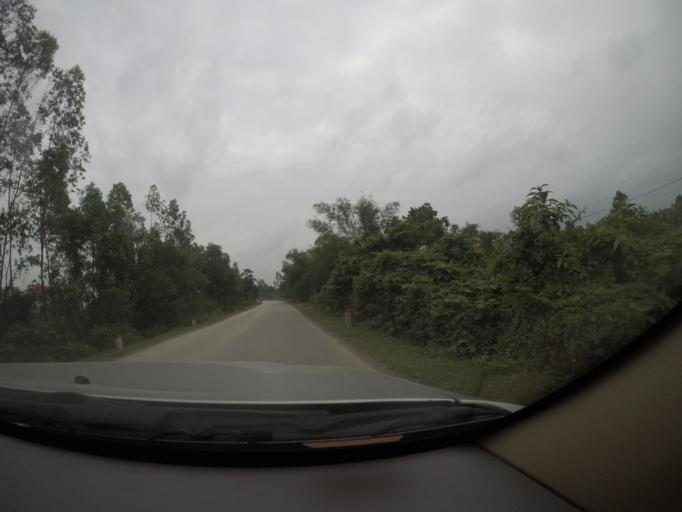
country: VN
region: Quang Binh
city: Quan Hau
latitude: 17.2894
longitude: 106.6456
